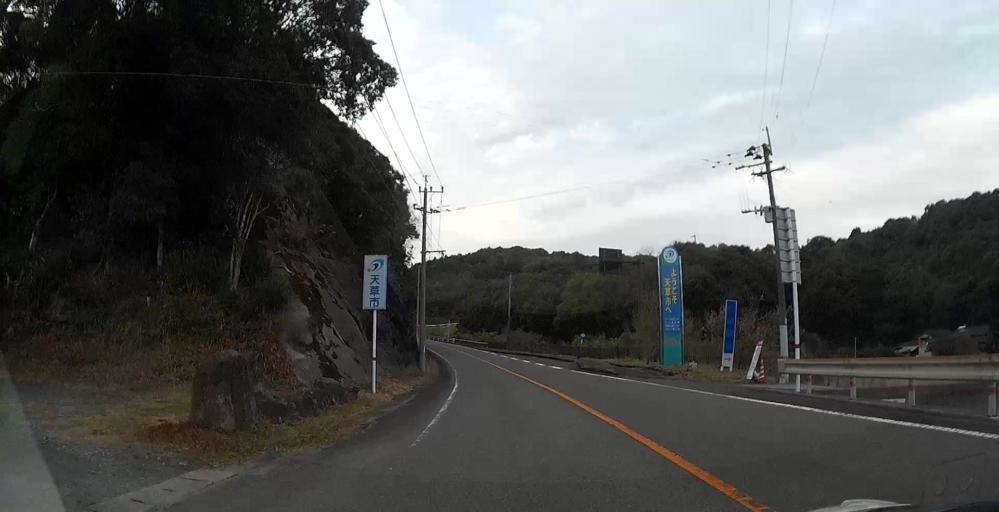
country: JP
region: Kumamoto
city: Hondo
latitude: 32.5046
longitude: 130.3894
